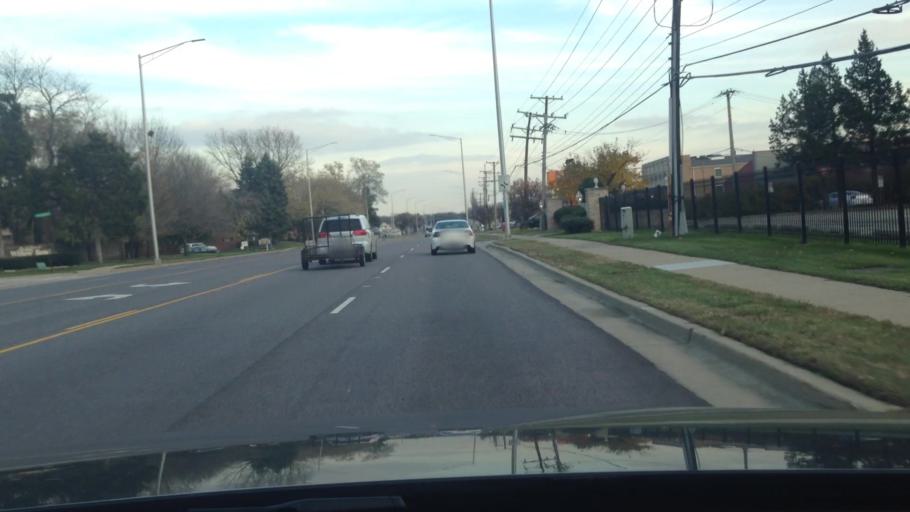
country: US
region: Illinois
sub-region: Cook County
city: Rolling Meadows
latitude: 42.0596
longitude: -88.0142
